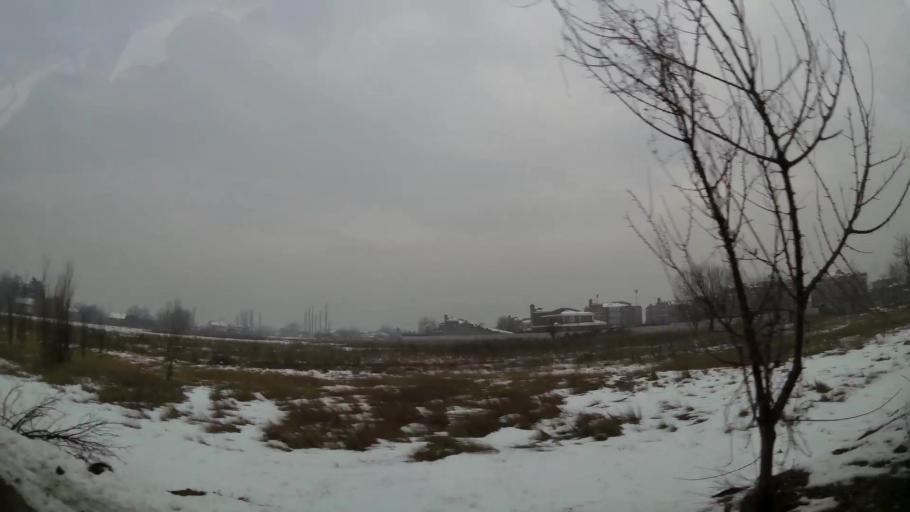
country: MK
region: Cucer-Sandevo
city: Chucher - Sandevo
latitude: 42.0496
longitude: 21.3654
